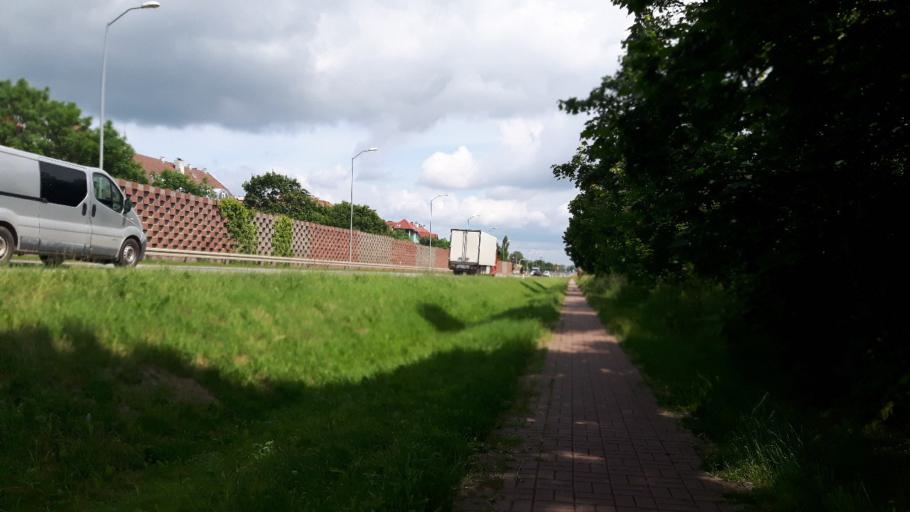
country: PL
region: West Pomeranian Voivodeship
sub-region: Powiat policki
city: Przeclaw
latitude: 53.3792
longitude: 14.4765
